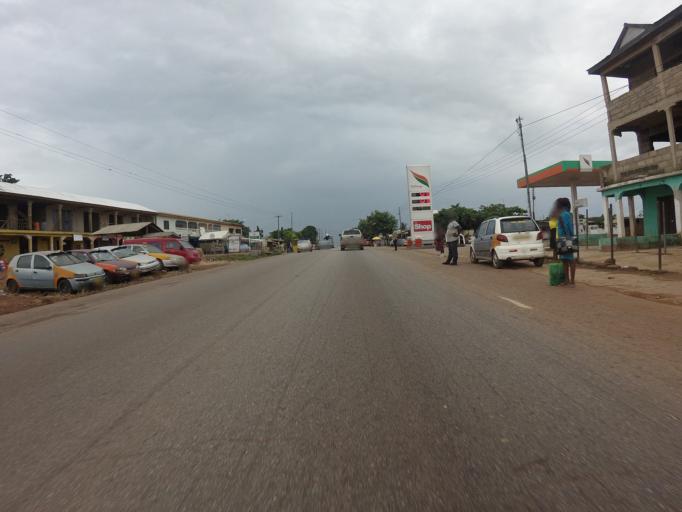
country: GH
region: Ashanti
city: Konongo
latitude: 6.6209
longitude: -1.1963
